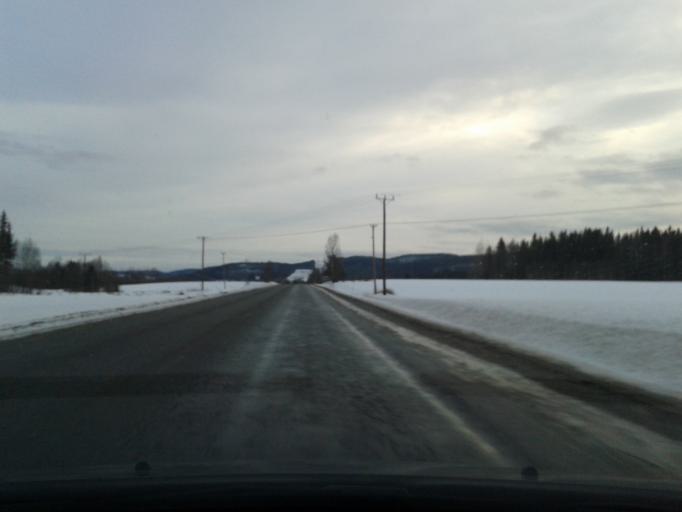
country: SE
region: Vaesternorrland
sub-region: Solleftea Kommun
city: Solleftea
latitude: 63.2507
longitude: 17.2133
